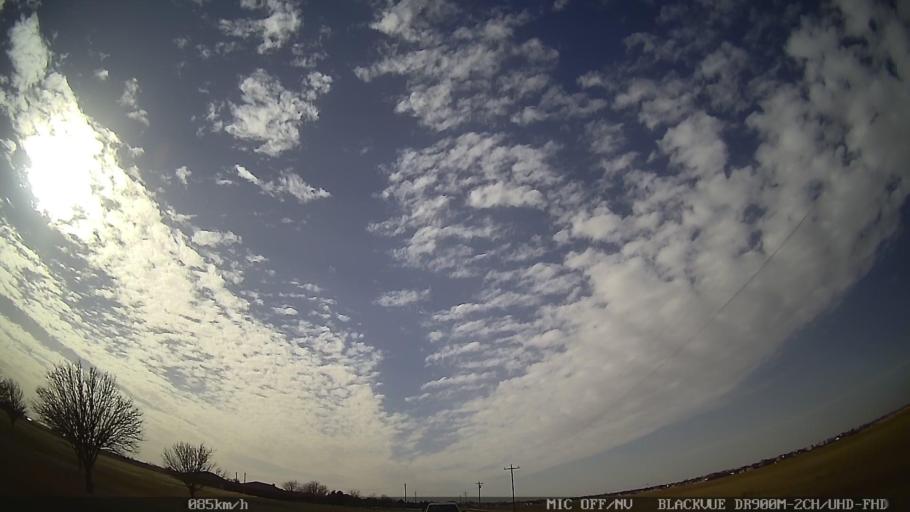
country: US
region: New Mexico
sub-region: Curry County
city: Clovis
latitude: 34.4194
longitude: -103.1539
